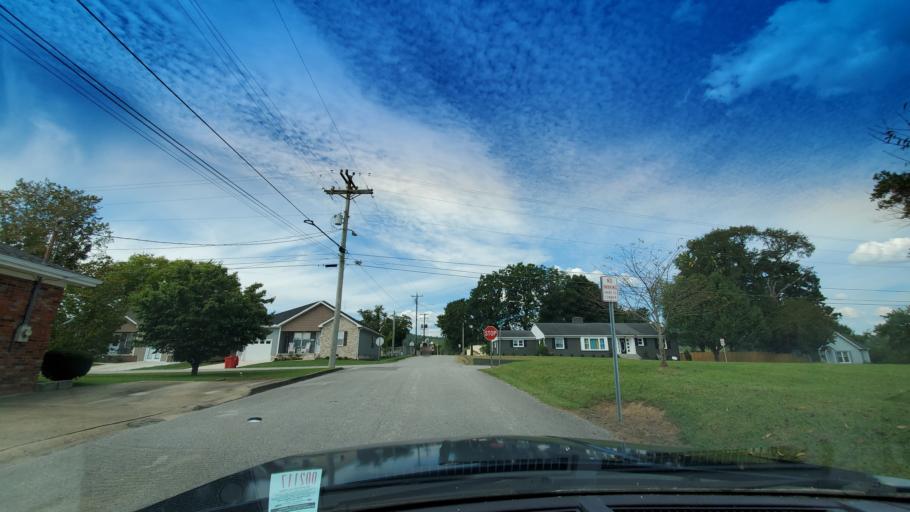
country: US
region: Tennessee
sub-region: Smith County
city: Carthage
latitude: 36.2516
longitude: -85.9488
